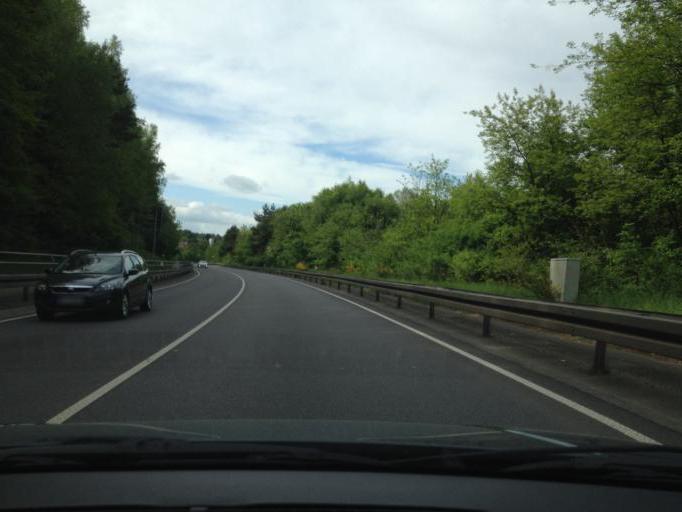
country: DE
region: Saarland
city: Bexbach
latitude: 49.3412
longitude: 7.2271
